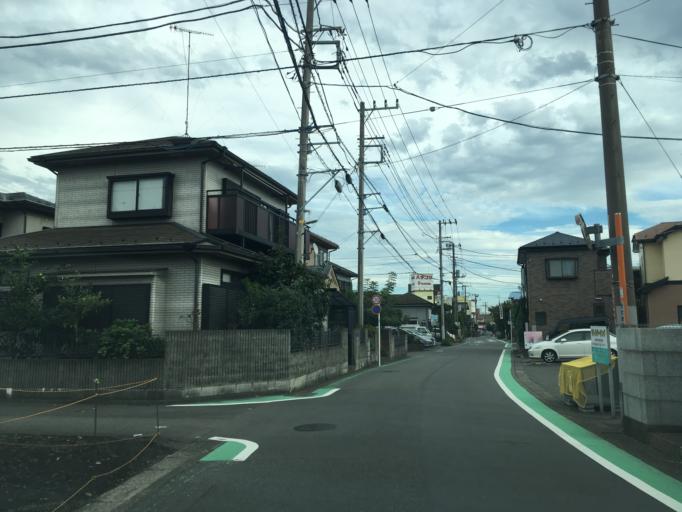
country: JP
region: Kanagawa
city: Zama
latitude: 35.5590
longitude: 139.3580
